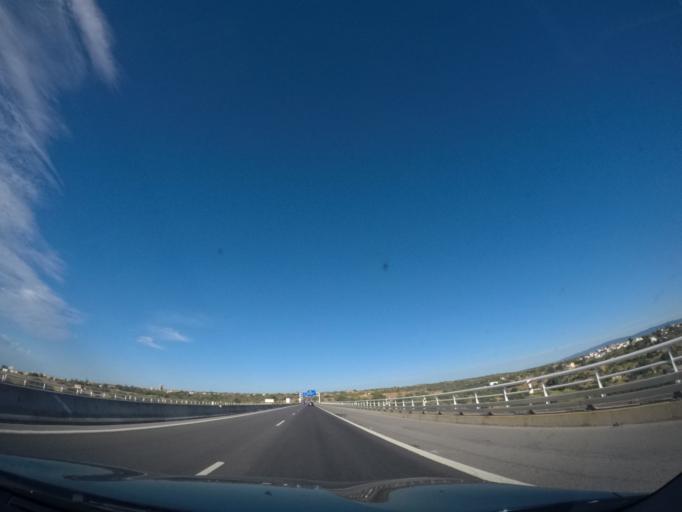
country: PT
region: Faro
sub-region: Silves
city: Armacao de Pera
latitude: 37.1376
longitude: -8.3430
